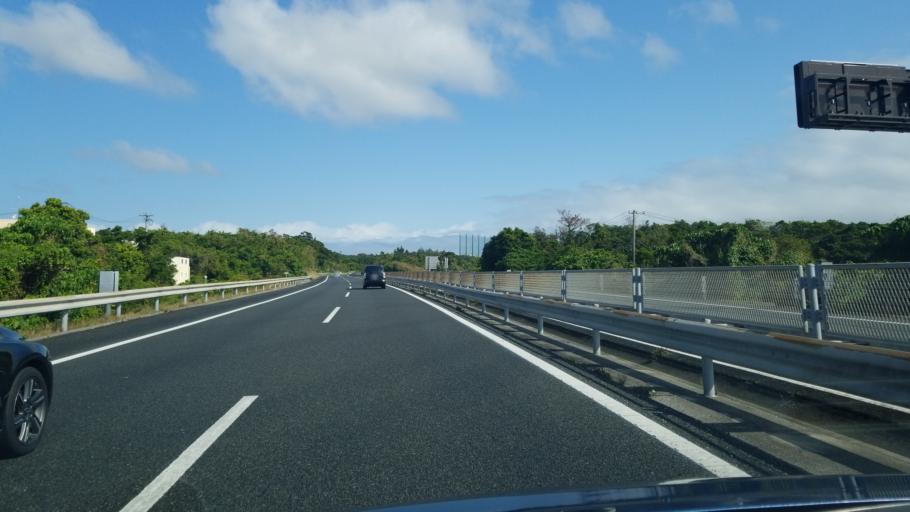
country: JP
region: Okinawa
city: Ishikawa
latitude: 26.3780
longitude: 127.8193
